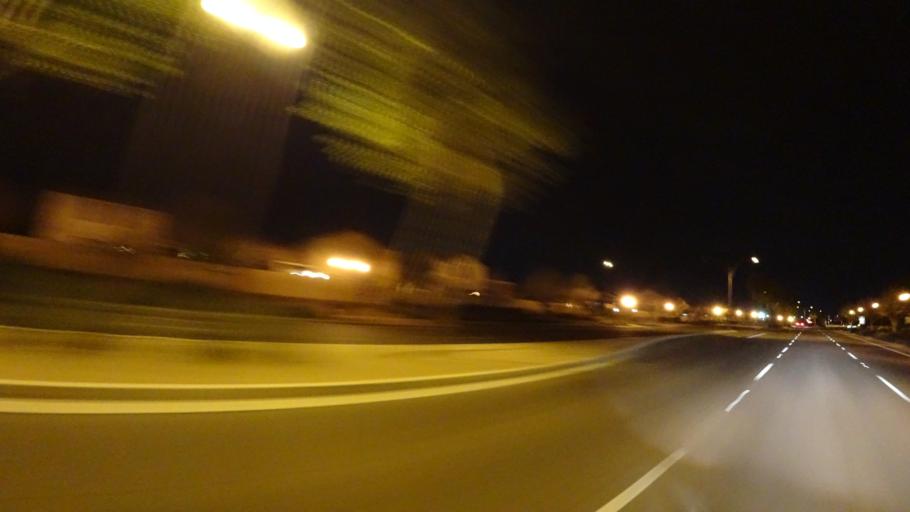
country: US
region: Arizona
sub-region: Maricopa County
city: Gilbert
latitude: 33.3214
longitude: -111.7326
